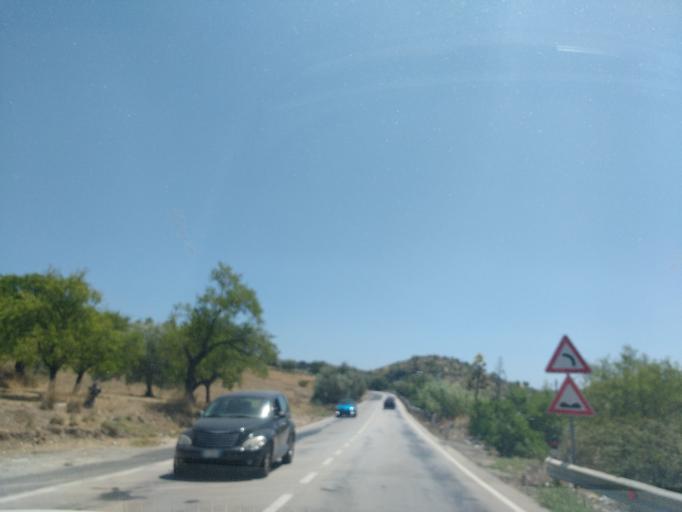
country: IT
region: Sicily
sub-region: Provincia di Siracusa
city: Noto
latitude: 36.8675
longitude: 15.0292
